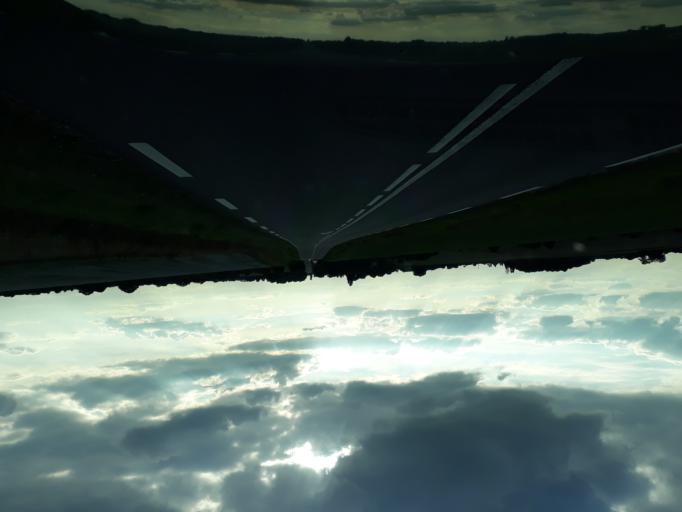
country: FR
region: Centre
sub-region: Departement du Loir-et-Cher
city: Aze
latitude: 47.8974
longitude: 0.9698
